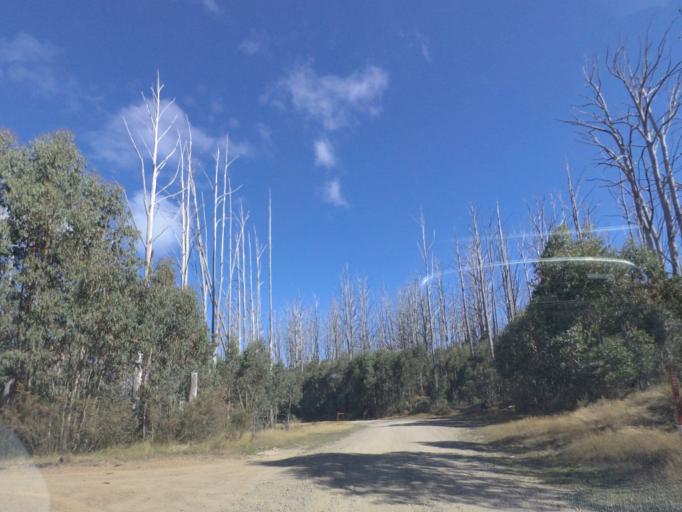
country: AU
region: Victoria
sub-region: Murrindindi
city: Alexandra
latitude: -37.4388
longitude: 145.8022
